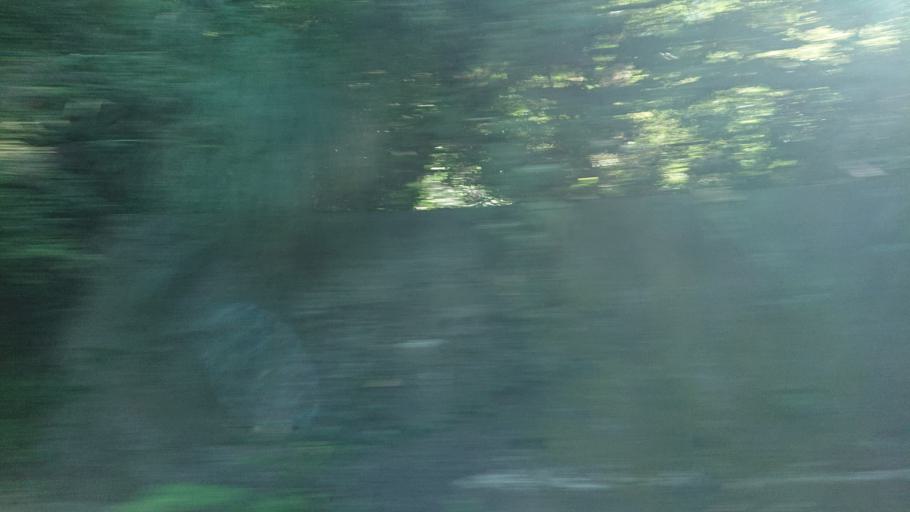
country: TW
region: Taiwan
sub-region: Chiayi
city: Jiayi Shi
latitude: 23.5333
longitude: 120.6295
